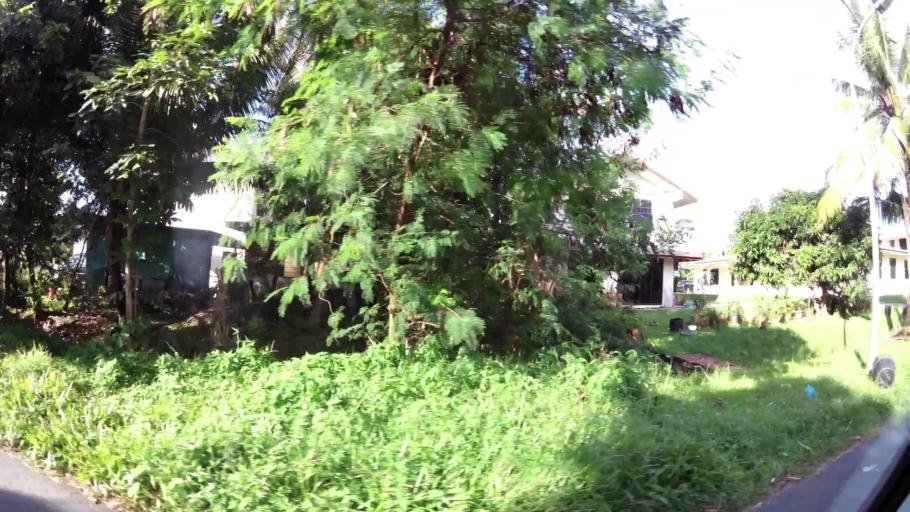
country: BN
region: Brunei and Muara
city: Bandar Seri Begawan
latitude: 4.9870
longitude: 114.9698
